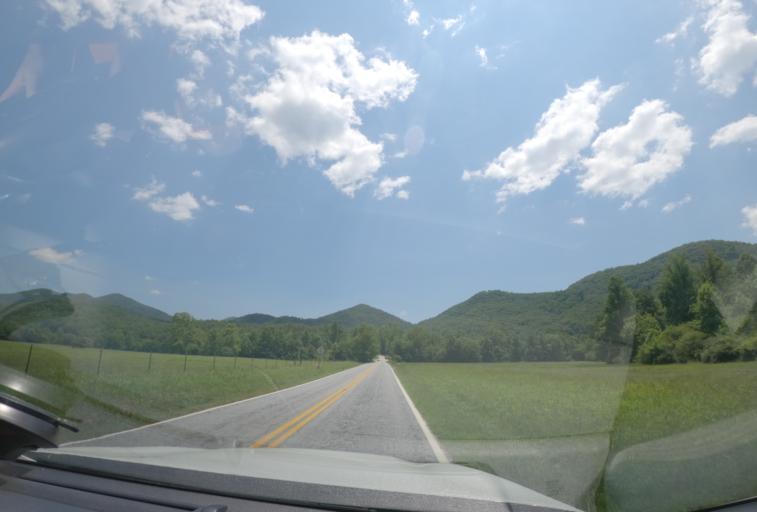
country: US
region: South Carolina
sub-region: Pickens County
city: Pickens
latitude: 34.9962
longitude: -82.8302
